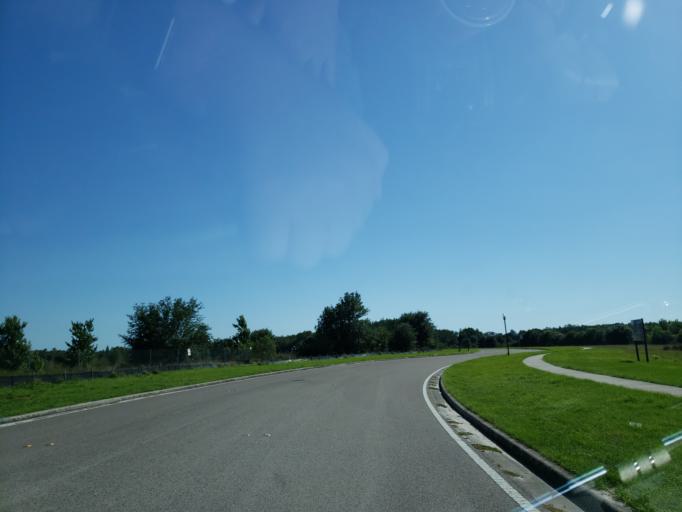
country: US
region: Florida
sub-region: Pasco County
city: Wesley Chapel
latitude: 28.2275
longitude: -82.3585
